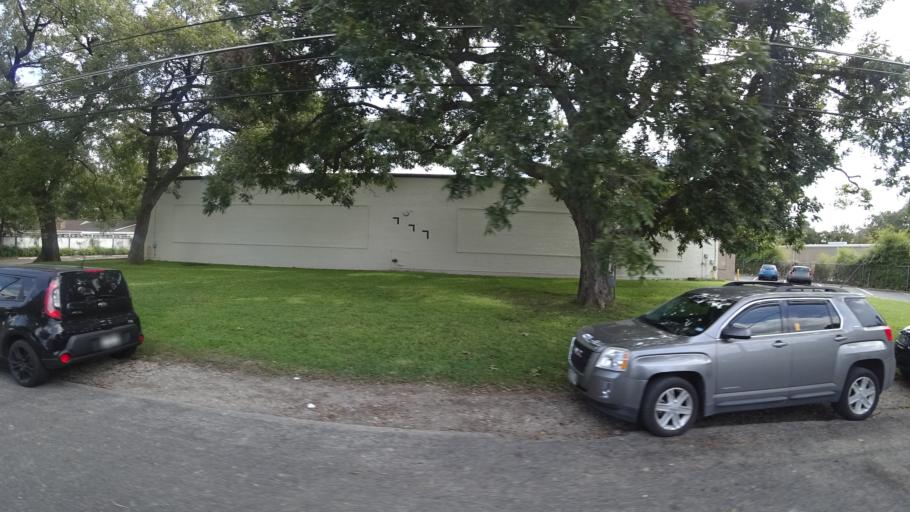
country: US
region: Texas
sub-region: Travis County
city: Austin
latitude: 30.2556
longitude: -97.6961
